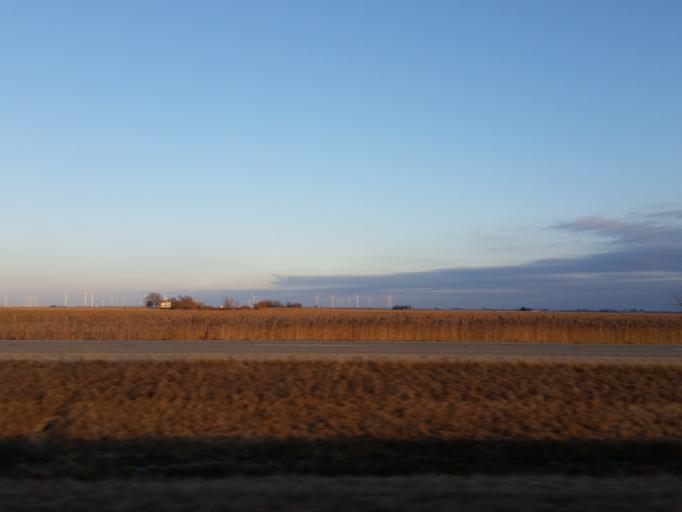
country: US
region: Illinois
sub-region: Woodford County
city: Minonk
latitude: 40.8374
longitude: -89.0363
